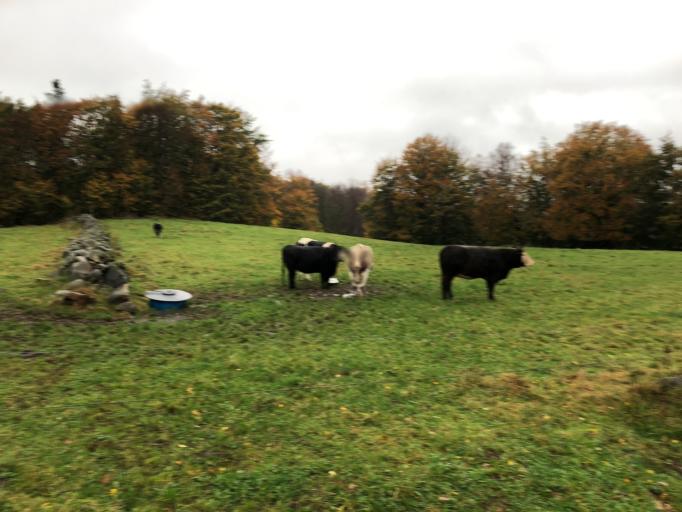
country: SE
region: Skane
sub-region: Kristianstads Kommun
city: Degeberga
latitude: 55.8688
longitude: 13.9021
